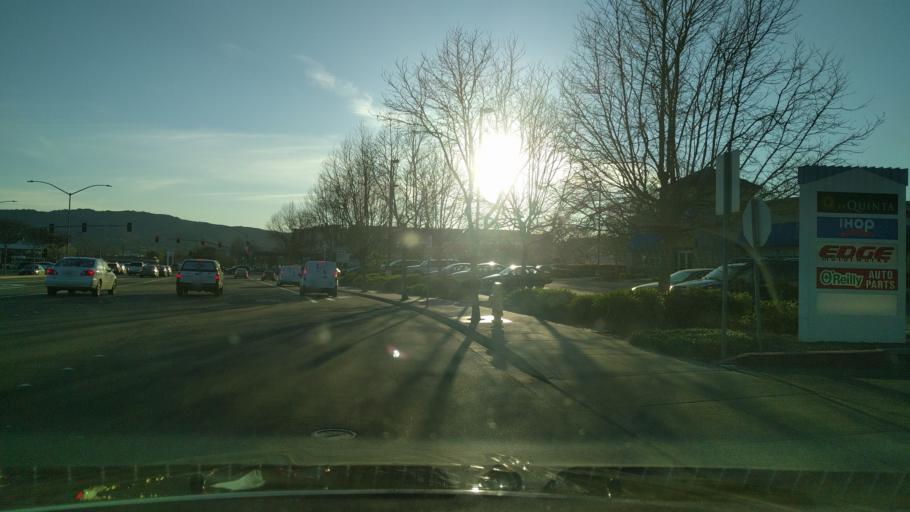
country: US
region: California
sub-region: Alameda County
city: Dublin
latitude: 37.7057
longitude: -121.9083
